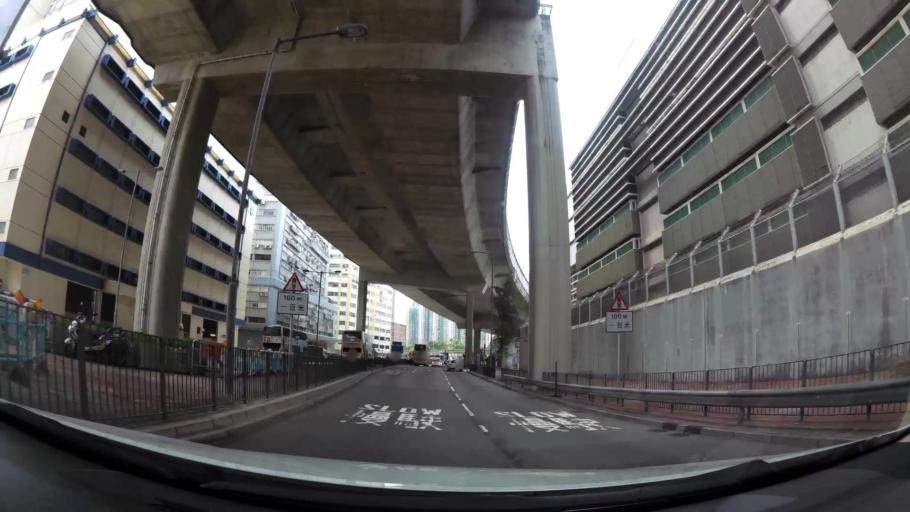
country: HK
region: Sham Shui Po
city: Sham Shui Po
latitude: 22.3383
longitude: 114.1444
